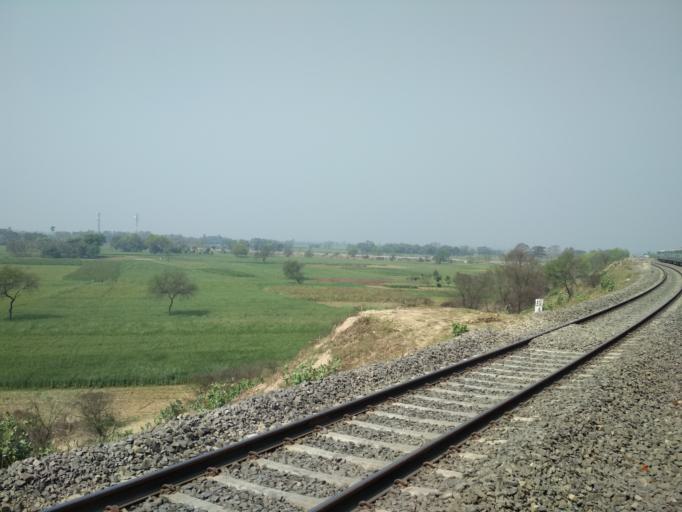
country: IN
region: Bihar
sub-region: Munger
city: Munger
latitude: 25.4347
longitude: 86.4374
